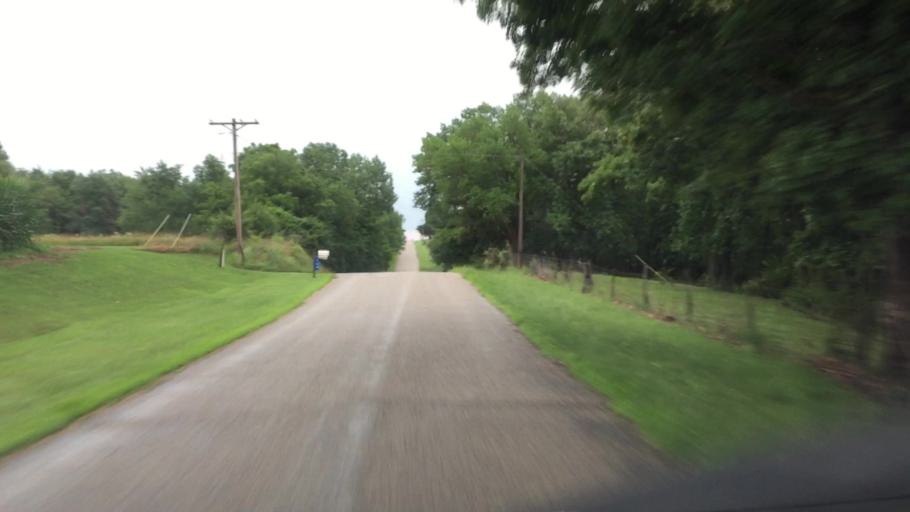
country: US
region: Illinois
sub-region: Hancock County
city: Hamilton
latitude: 40.4263
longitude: -91.3570
